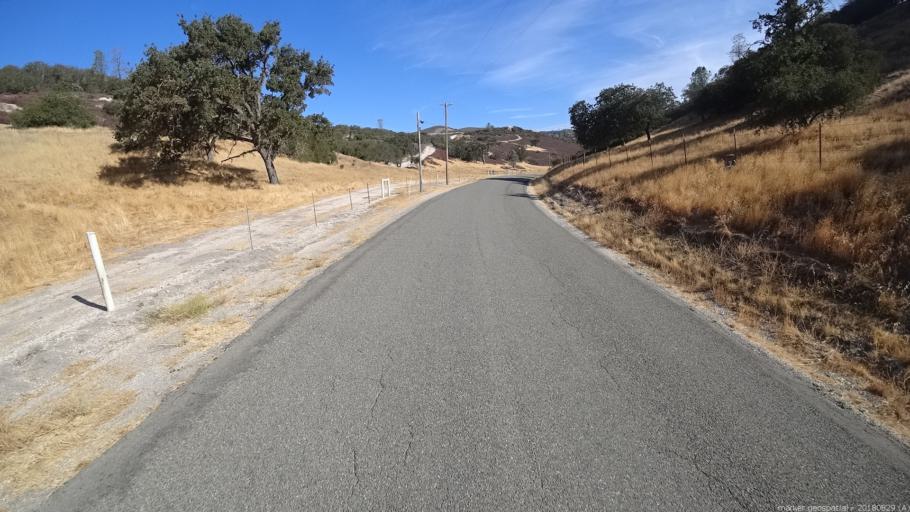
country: US
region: California
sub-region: Monterey County
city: King City
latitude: 35.9818
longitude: -121.0811
